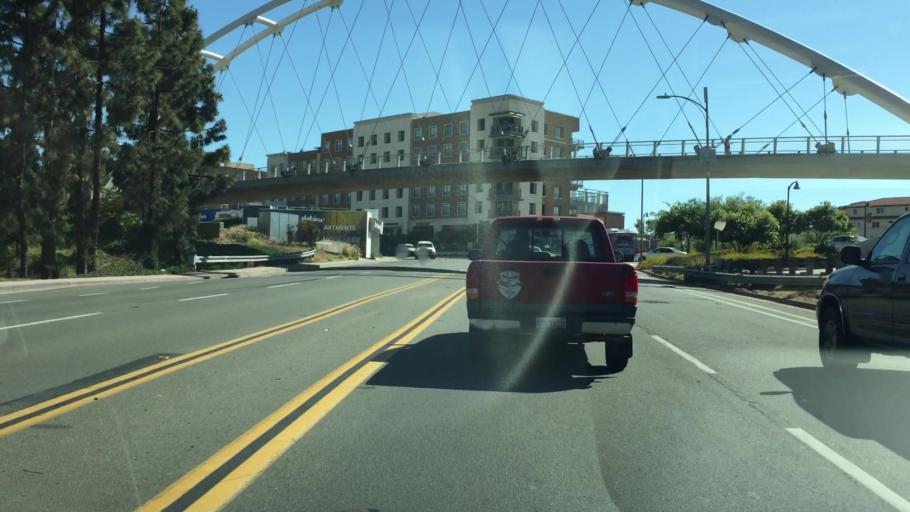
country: US
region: California
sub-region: San Diego County
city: La Mesa
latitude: 32.7734
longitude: -117.0690
